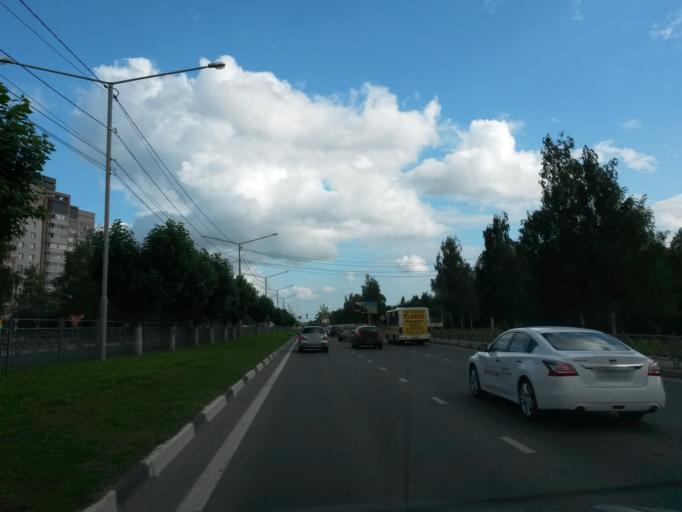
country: RU
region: Jaroslavl
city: Yaroslavl
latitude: 57.5830
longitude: 39.9090
